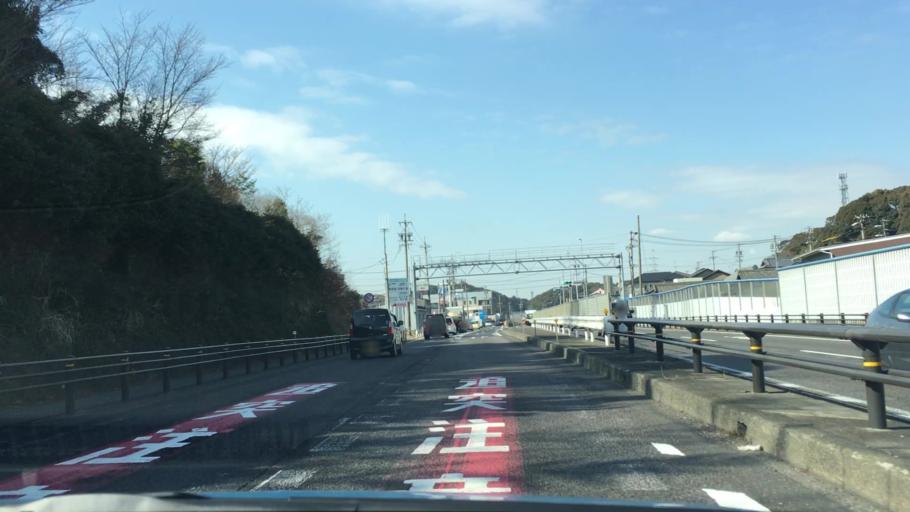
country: JP
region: Aichi
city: Gamagori
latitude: 34.8987
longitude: 137.2432
